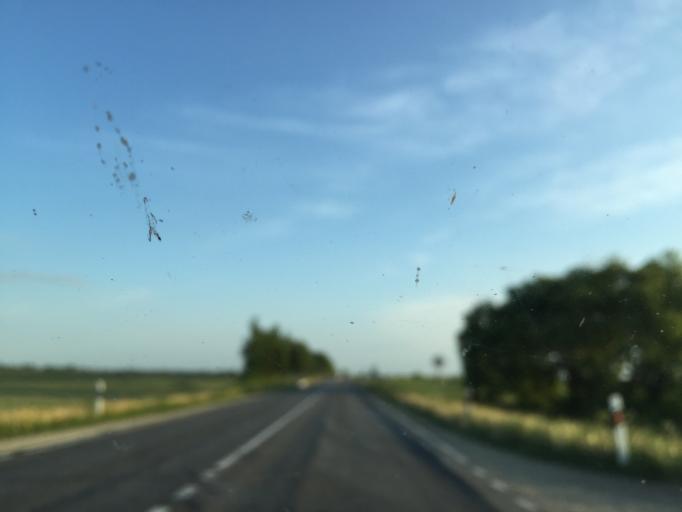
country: LT
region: Siauliu apskritis
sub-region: Joniskis
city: Joniskis
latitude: 56.0885
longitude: 23.4678
